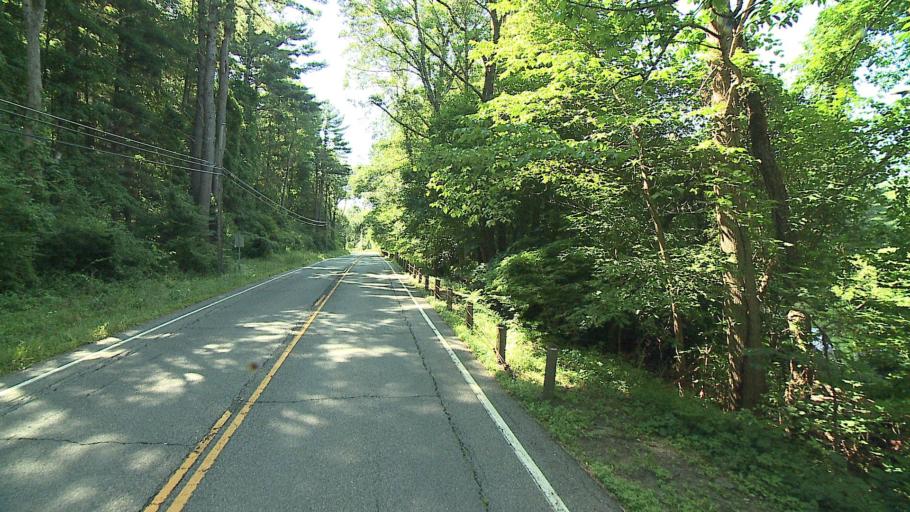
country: US
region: Connecticut
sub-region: Litchfield County
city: Canaan
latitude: 42.0154
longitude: -73.4294
